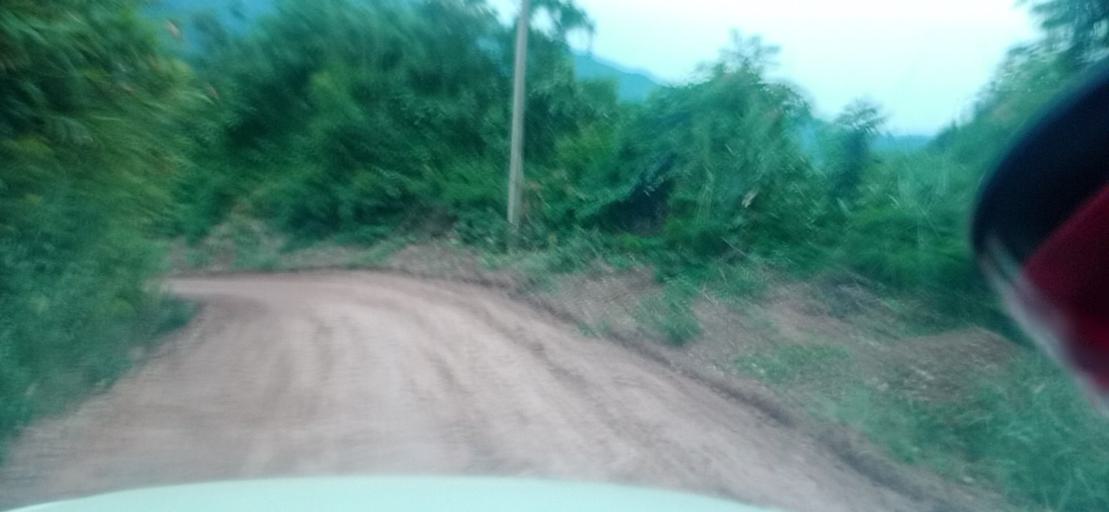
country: TH
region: Changwat Bueng Kan
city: Pak Khat
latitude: 18.5517
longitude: 103.4281
